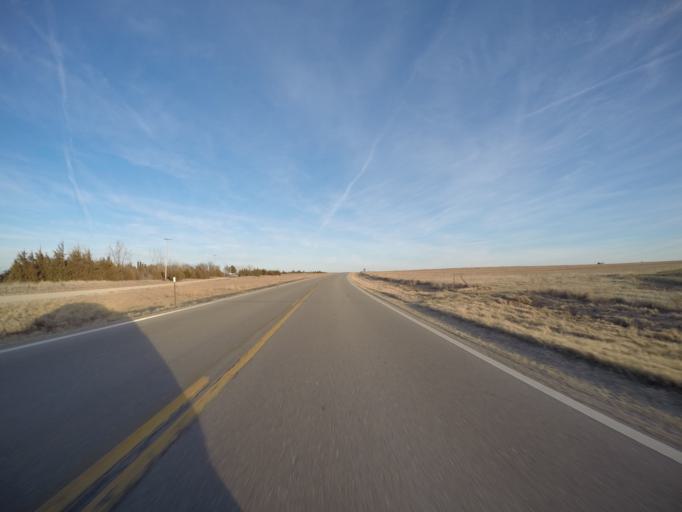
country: US
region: Kansas
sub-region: Dickinson County
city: Herington
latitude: 38.6673
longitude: -96.8865
